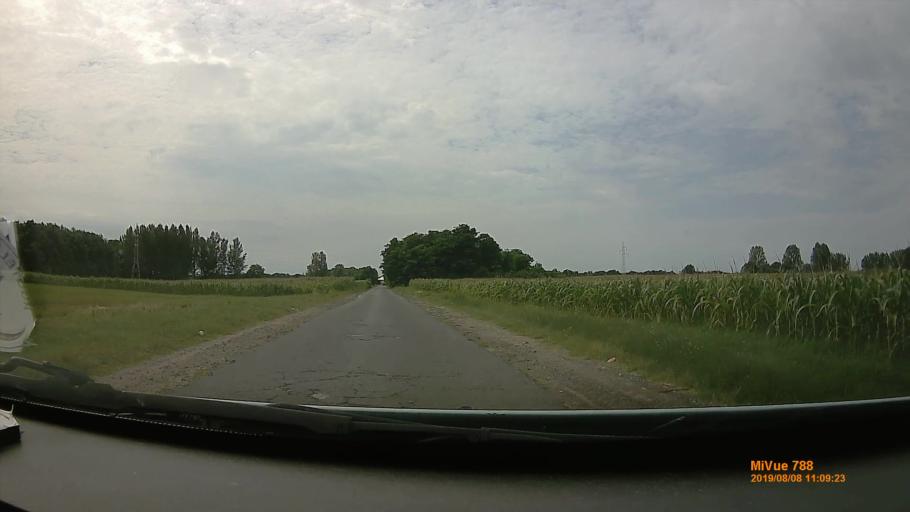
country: HU
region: Szabolcs-Szatmar-Bereg
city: Balkany
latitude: 47.7529
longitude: 21.8445
